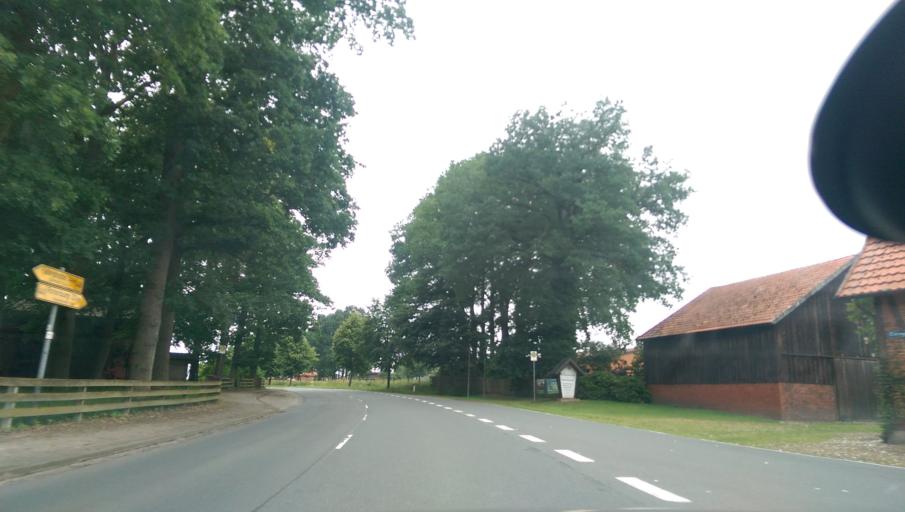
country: DE
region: Lower Saxony
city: Visselhovede
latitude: 52.9668
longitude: 9.6254
